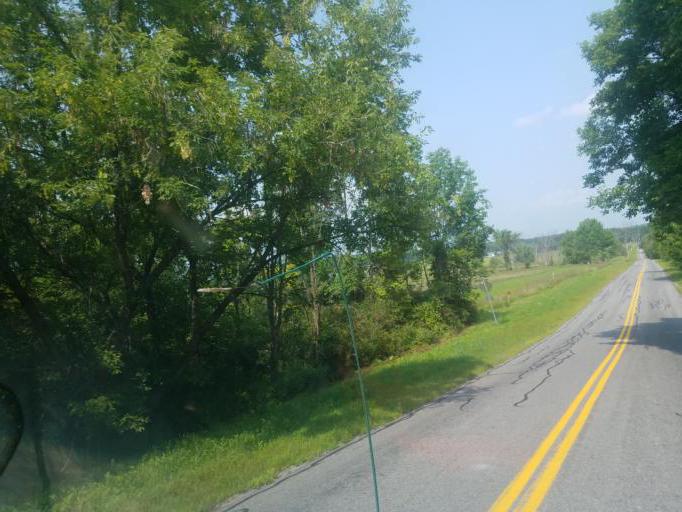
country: US
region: New York
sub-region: Montgomery County
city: Fonda
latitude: 42.8563
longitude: -74.3707
